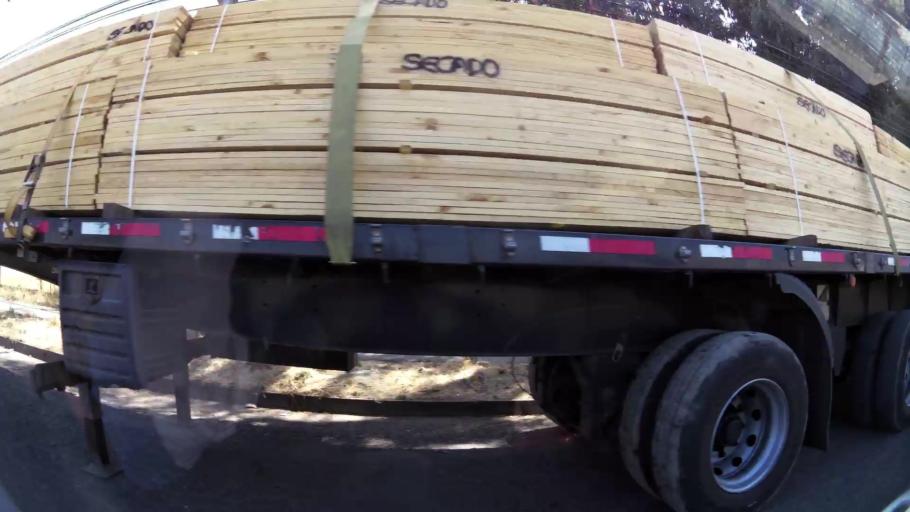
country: CL
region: Maule
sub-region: Provincia de Talca
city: Talca
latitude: -35.4235
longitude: -71.6380
